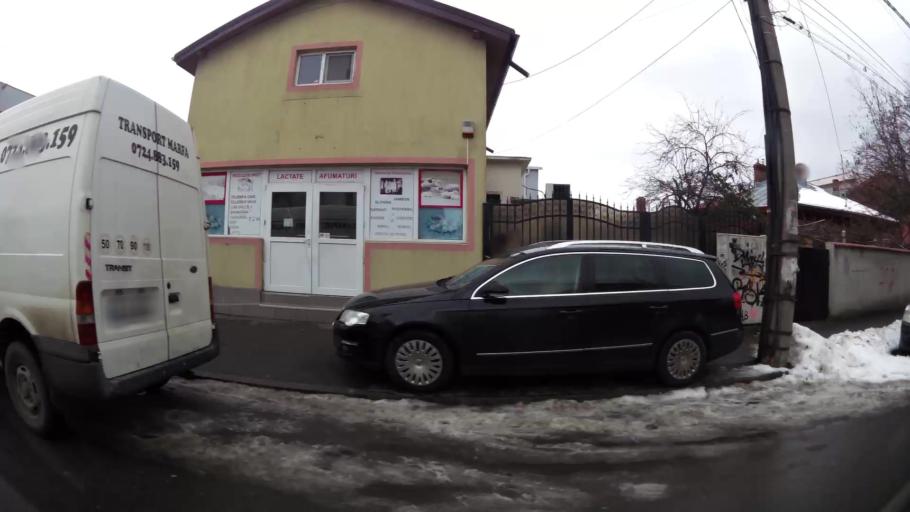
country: RO
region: Ilfov
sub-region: Comuna Pantelimon
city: Pantelimon
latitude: 44.4334
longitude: 26.2000
